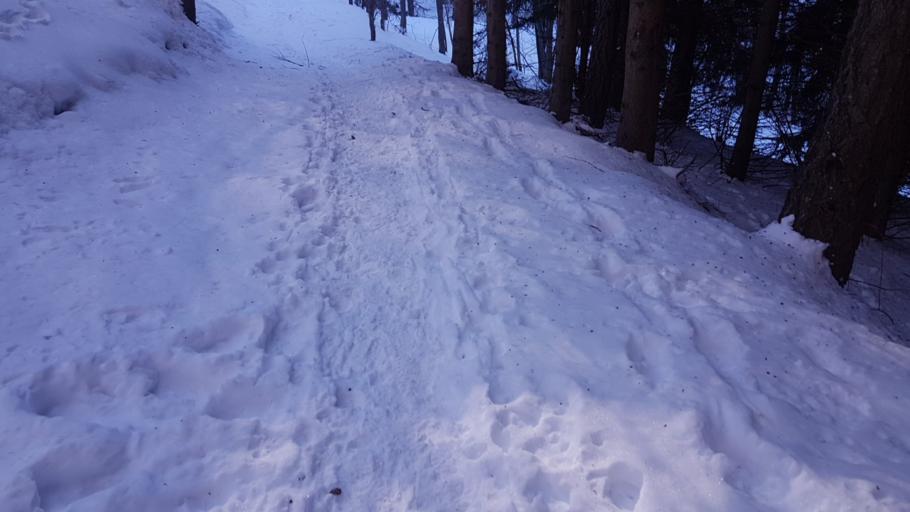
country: IT
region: Piedmont
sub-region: Provincia di Torino
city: Cesana Torinese
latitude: 44.9813
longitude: 6.8130
